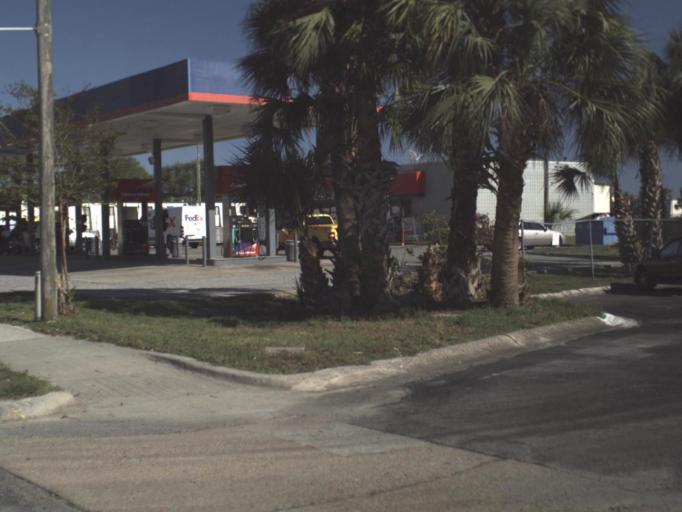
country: US
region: Florida
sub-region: Okaloosa County
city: Fort Walton Beach
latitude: 30.4065
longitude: -86.6330
